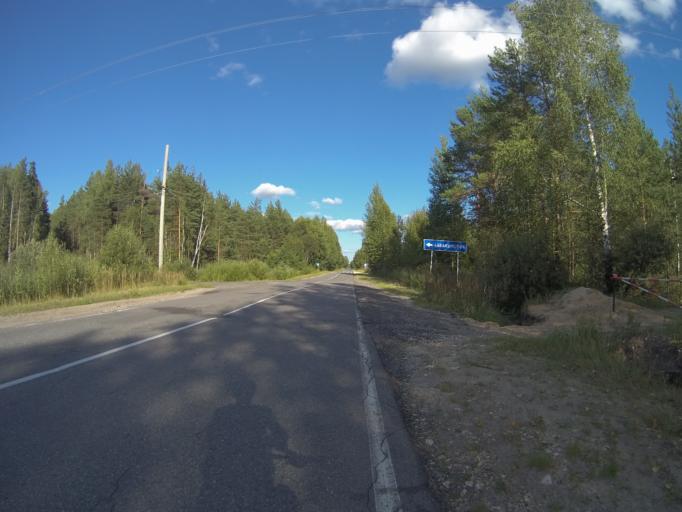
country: RU
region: Vladimir
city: Mezinovskiy
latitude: 55.5955
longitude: 40.3749
